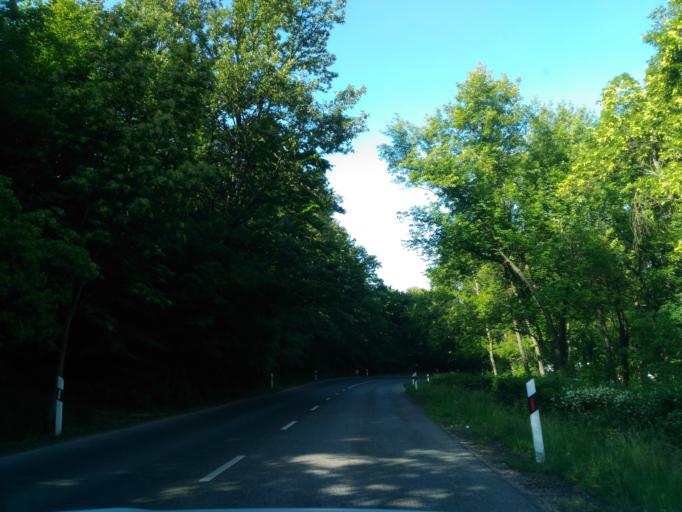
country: HU
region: Baranya
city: Komlo
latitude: 46.1812
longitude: 18.2611
